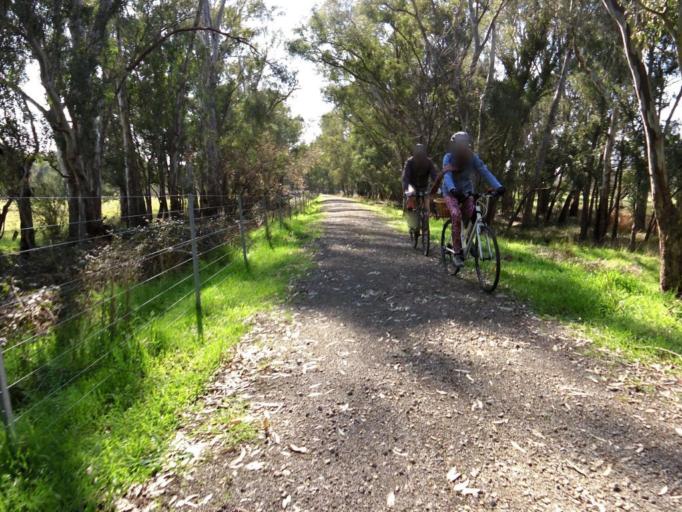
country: AU
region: Victoria
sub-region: Murrindindi
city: Alexandra
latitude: -37.1562
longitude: 145.5732
